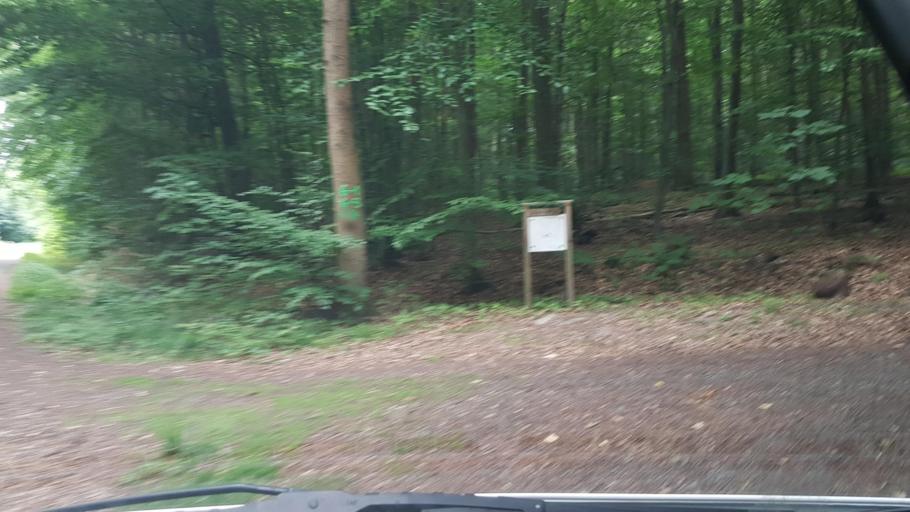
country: DE
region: Lower Saxony
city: Warberg
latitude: 52.1720
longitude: 10.9025
